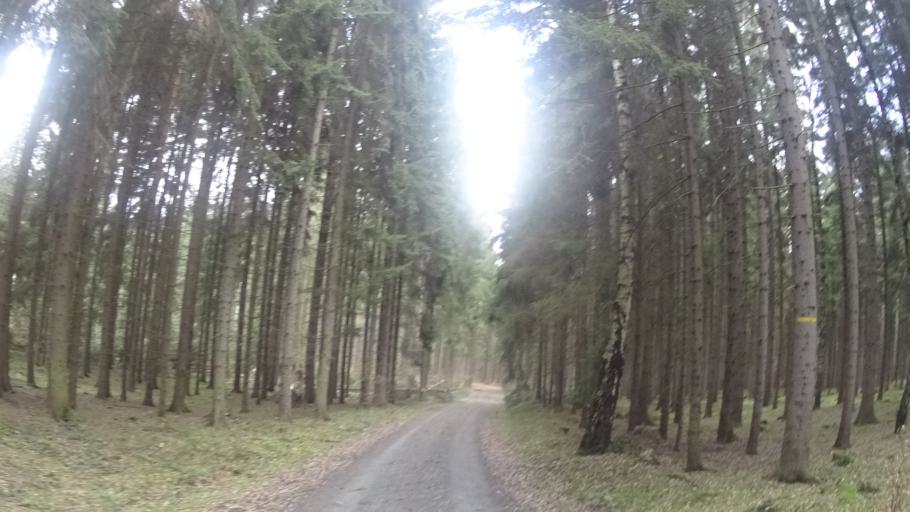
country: DE
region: Thuringia
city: Zeulenroda
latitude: 50.6296
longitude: 12.0035
